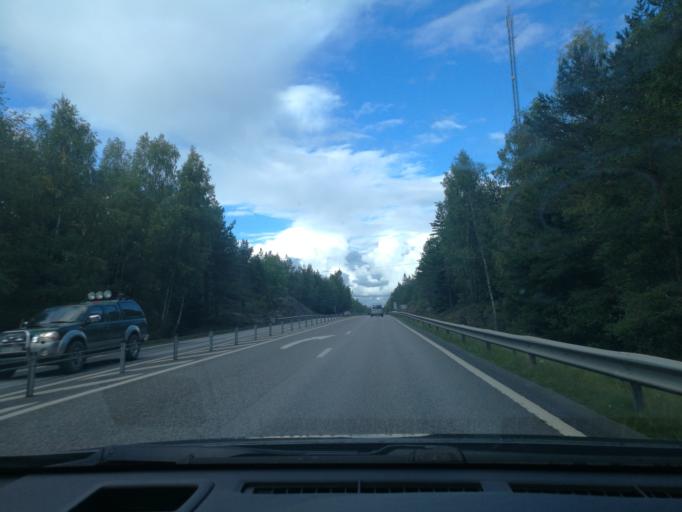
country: SE
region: OEstergoetland
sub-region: Norrkopings Kommun
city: Jursla
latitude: 58.7093
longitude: 16.1601
